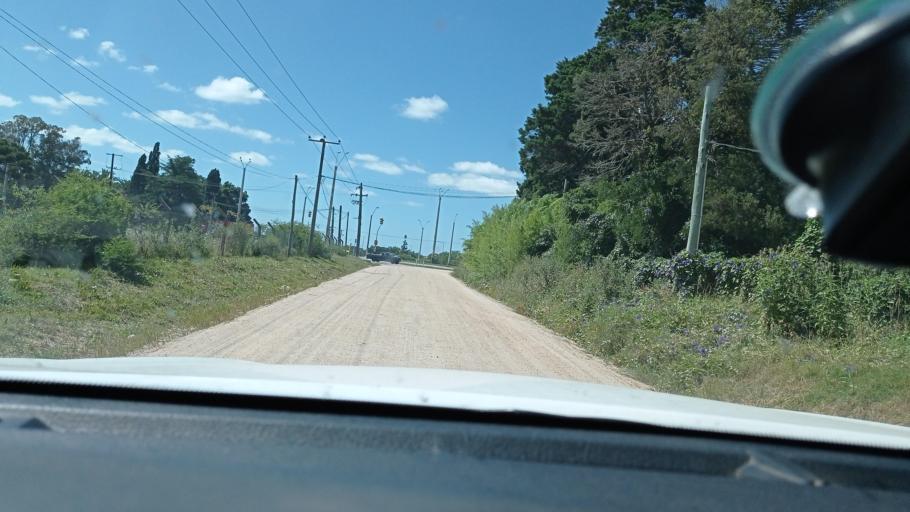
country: UY
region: Canelones
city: Pando
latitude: -34.7335
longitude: -55.9761
